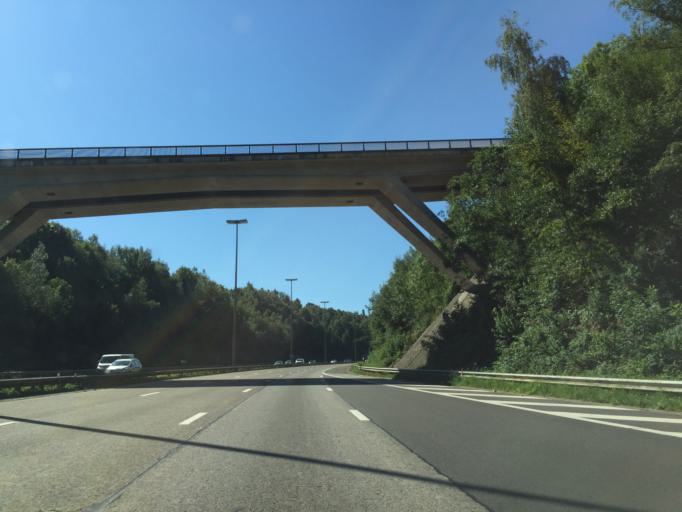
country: BE
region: Wallonia
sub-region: Province de Liege
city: Verviers
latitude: 50.5759
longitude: 5.8574
